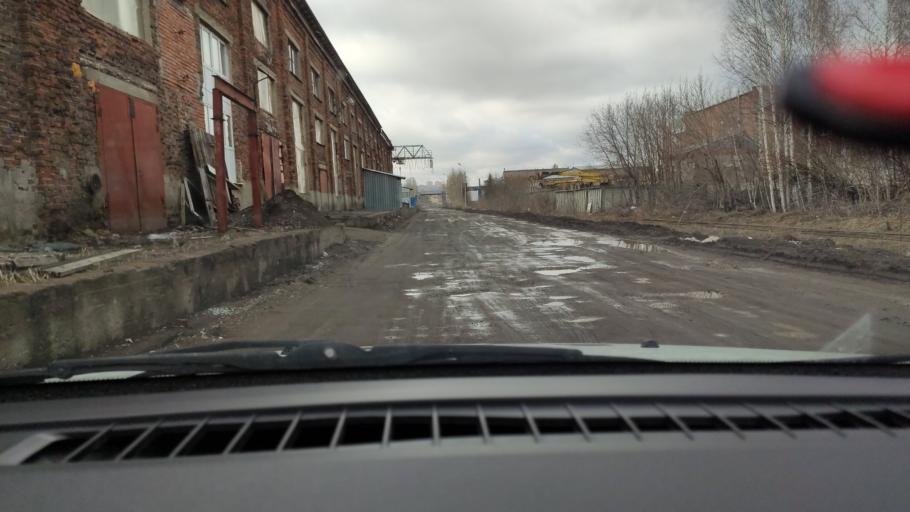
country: RU
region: Perm
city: Perm
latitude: 58.0494
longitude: 56.3182
